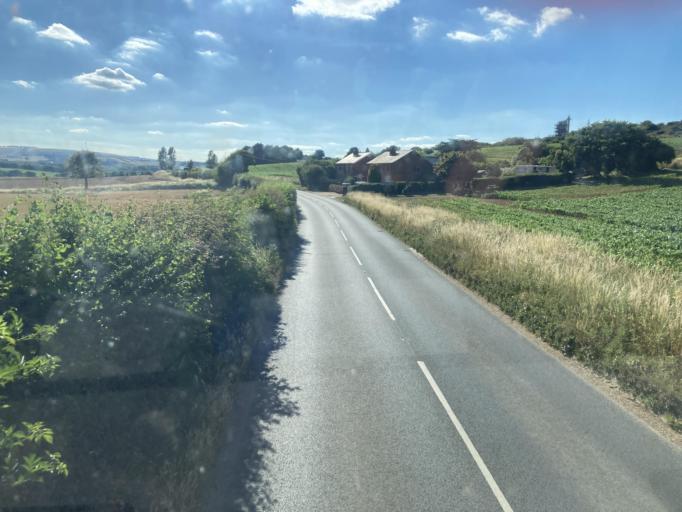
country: GB
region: England
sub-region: Isle of Wight
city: Newport
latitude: 50.6718
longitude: -1.2663
